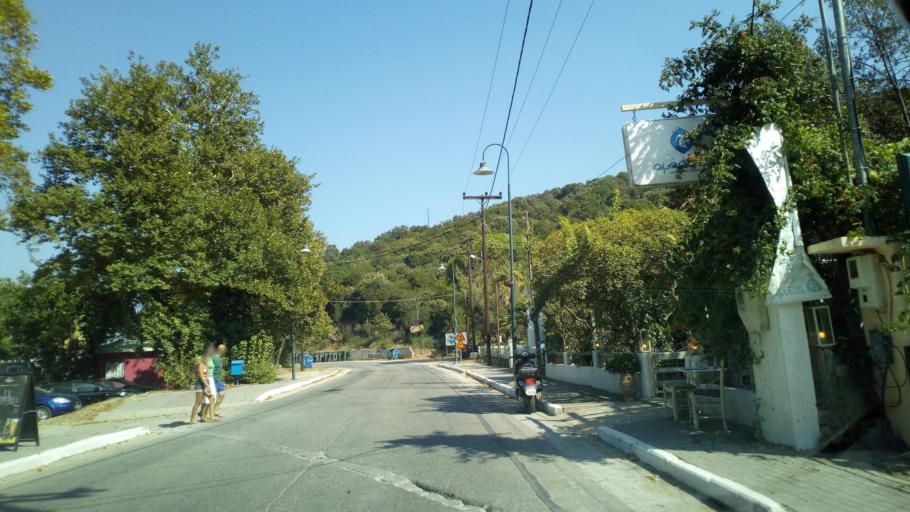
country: GR
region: Central Macedonia
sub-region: Nomos Thessalonikis
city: Stavros
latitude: 40.6629
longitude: 23.7079
